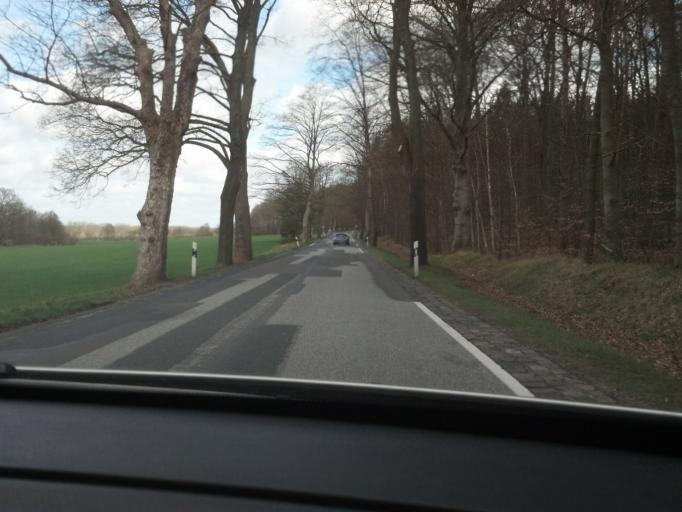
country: DE
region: Schleswig-Holstein
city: Langenlehsten
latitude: 53.4658
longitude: 10.7859
